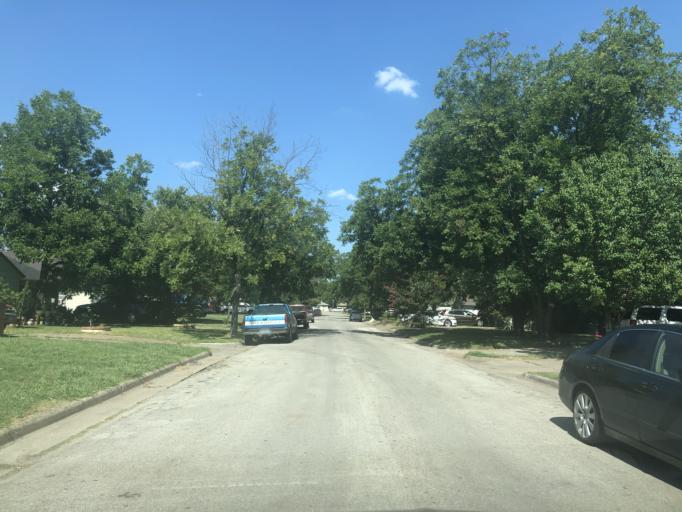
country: US
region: Texas
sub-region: Dallas County
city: Grand Prairie
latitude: 32.7365
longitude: -97.0114
